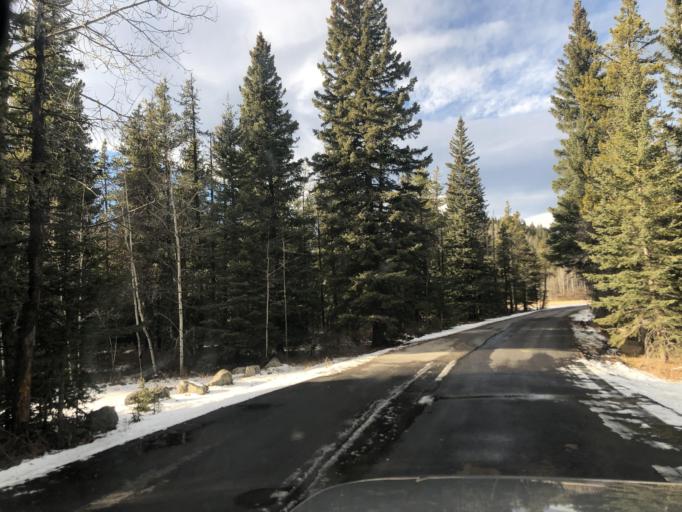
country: CA
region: Alberta
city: Cochrane
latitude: 51.0424
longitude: -114.8658
